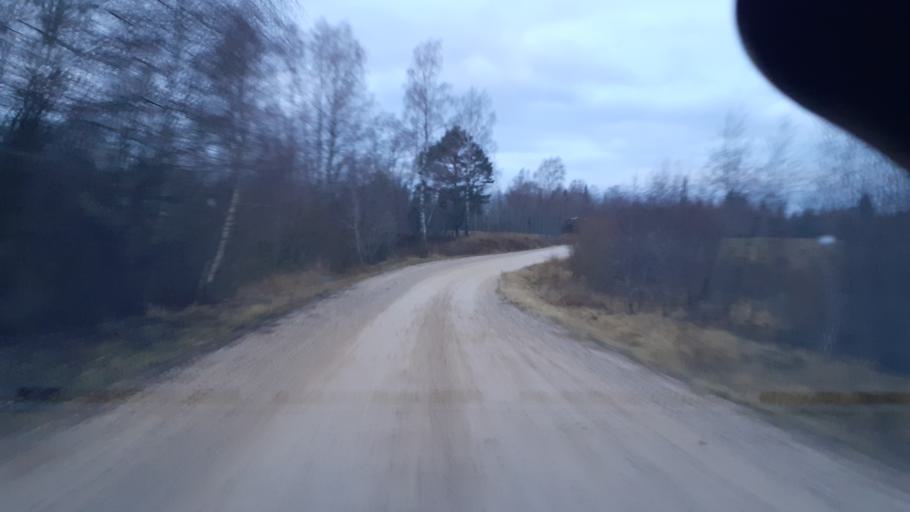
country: LV
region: Kuldigas Rajons
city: Kuldiga
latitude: 56.9549
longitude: 21.7975
